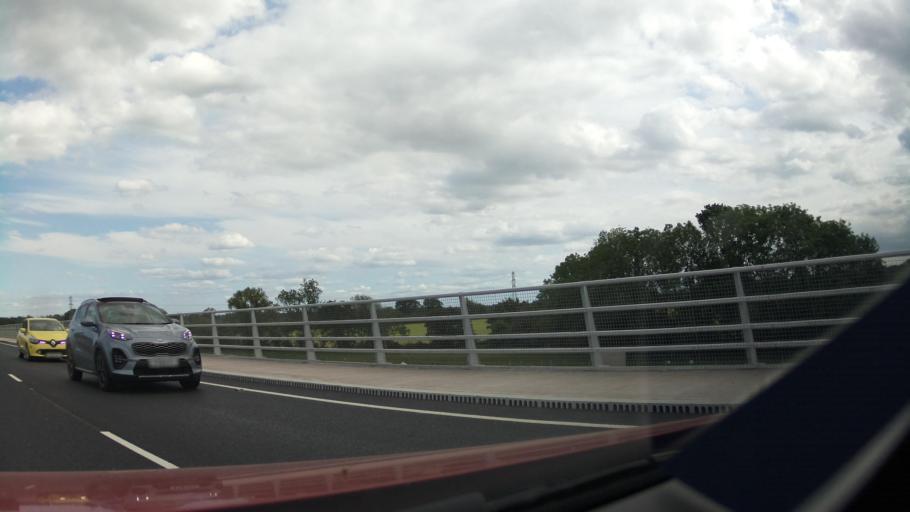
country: GB
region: England
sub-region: Worcestershire
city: Worcester
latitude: 52.1638
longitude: -2.2314
